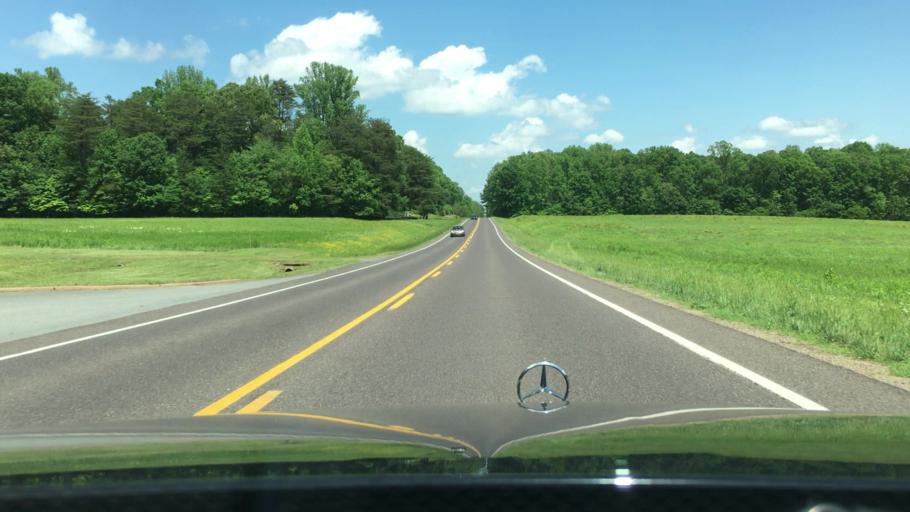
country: US
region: Virginia
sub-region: Spotsylvania County
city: Spotsylvania
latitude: 38.3157
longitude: -77.7565
